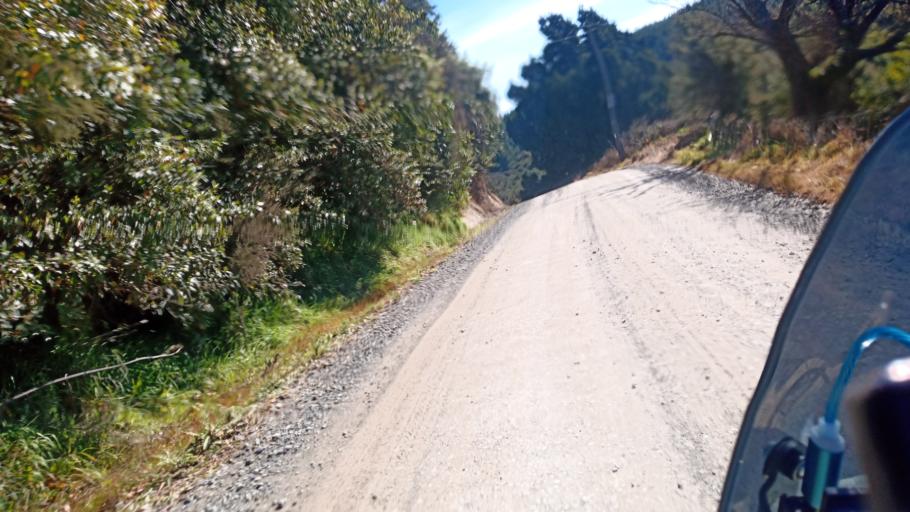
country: NZ
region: Gisborne
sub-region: Gisborne District
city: Gisborne
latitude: -37.9896
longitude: 178.2858
